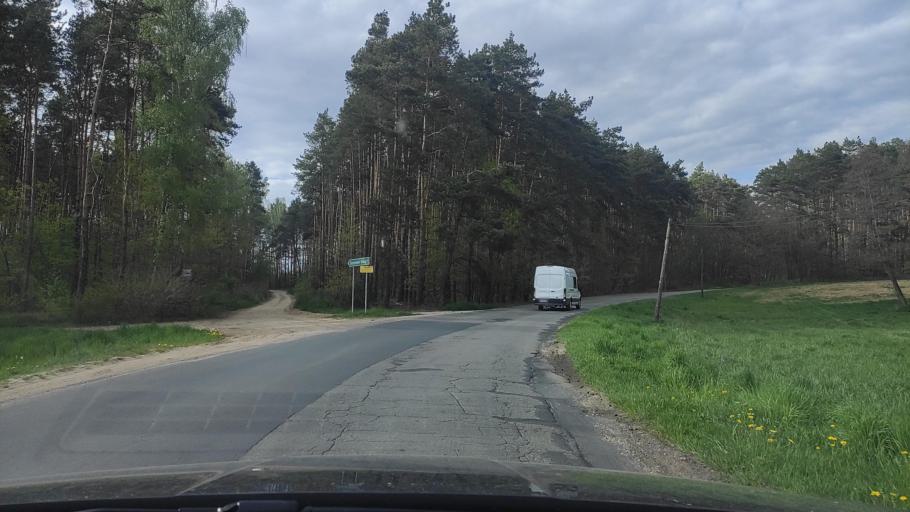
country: PL
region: Greater Poland Voivodeship
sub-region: Powiat poznanski
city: Kobylnica
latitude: 52.4509
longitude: 17.1605
